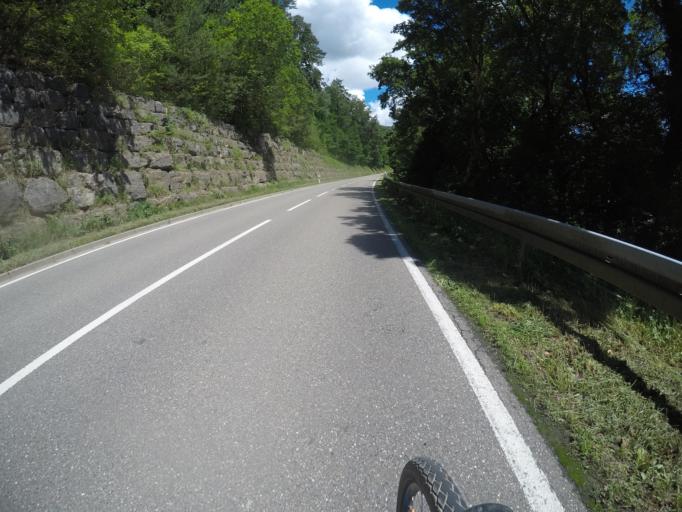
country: DE
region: Baden-Wuerttemberg
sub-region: Tuebingen Region
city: Hirrlingen
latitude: 48.4468
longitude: 8.8233
